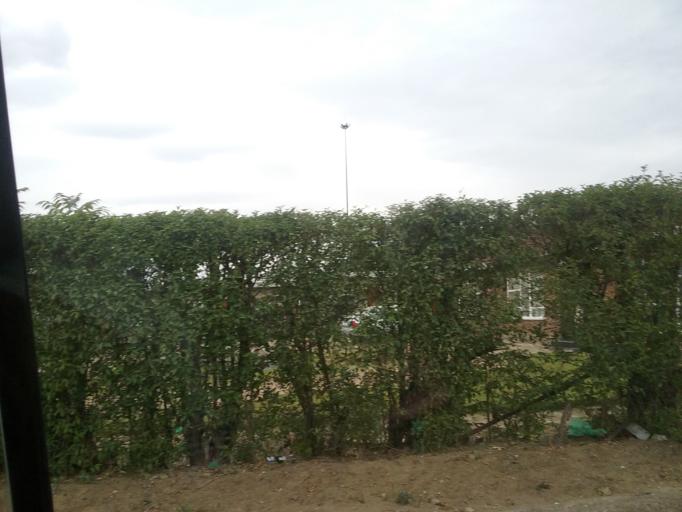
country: LS
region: Maseru
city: Maseru
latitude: -29.3200
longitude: 27.5105
